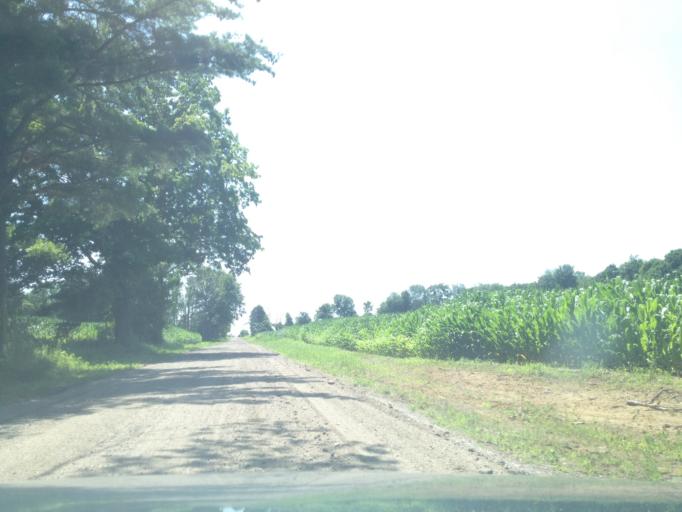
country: CA
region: Ontario
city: Aylmer
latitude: 42.6460
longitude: -80.7705
